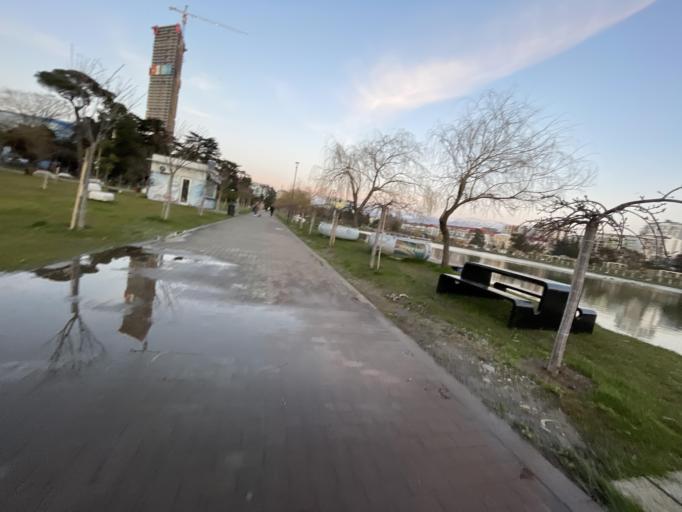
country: GE
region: Ajaria
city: Batumi
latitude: 41.6482
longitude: 41.6254
